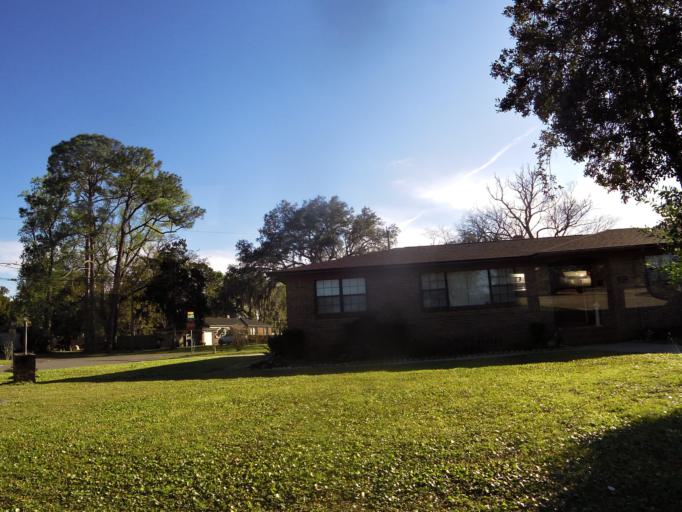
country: US
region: Florida
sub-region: Duval County
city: Jacksonville
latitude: 30.4037
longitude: -81.6738
